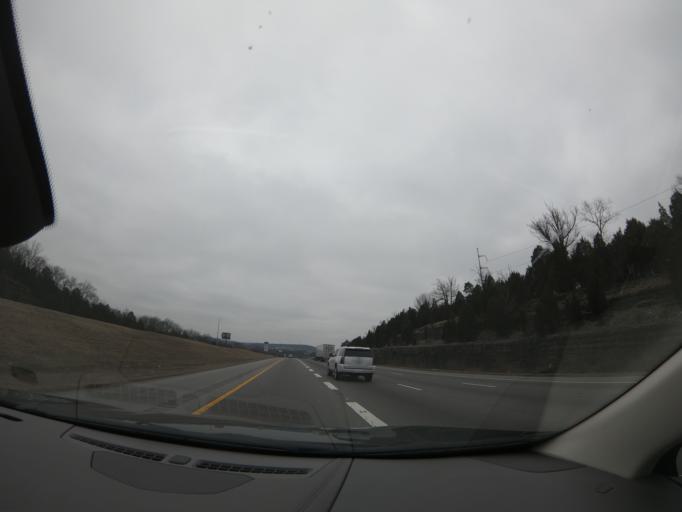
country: US
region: Tennessee
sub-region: Rutherford County
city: Smyrna
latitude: 35.9598
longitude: -86.5596
